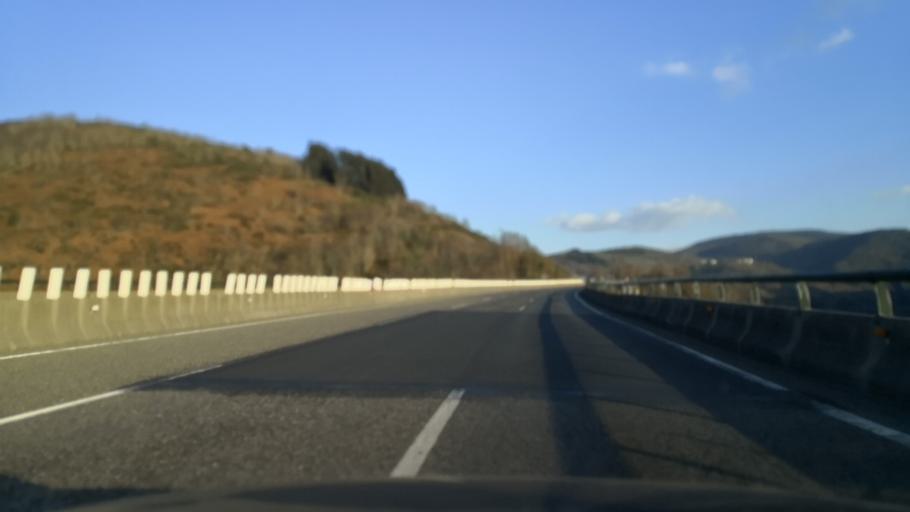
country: ES
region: Galicia
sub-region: Provincia de Lugo
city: San Roman
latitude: 42.7540
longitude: -7.0686
